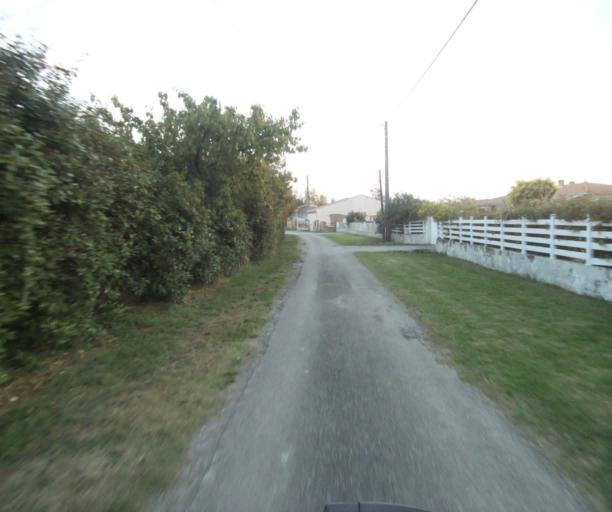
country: FR
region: Midi-Pyrenees
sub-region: Departement du Tarn-et-Garonne
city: Verdun-sur-Garonne
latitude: 43.8400
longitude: 1.2450
